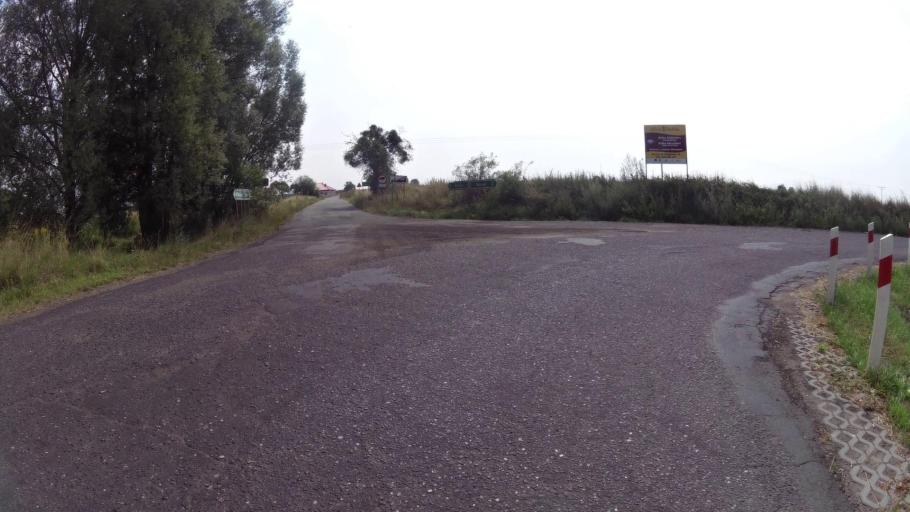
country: PL
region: West Pomeranian Voivodeship
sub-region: Powiat gryfinski
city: Moryn
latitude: 52.8526
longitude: 14.4223
